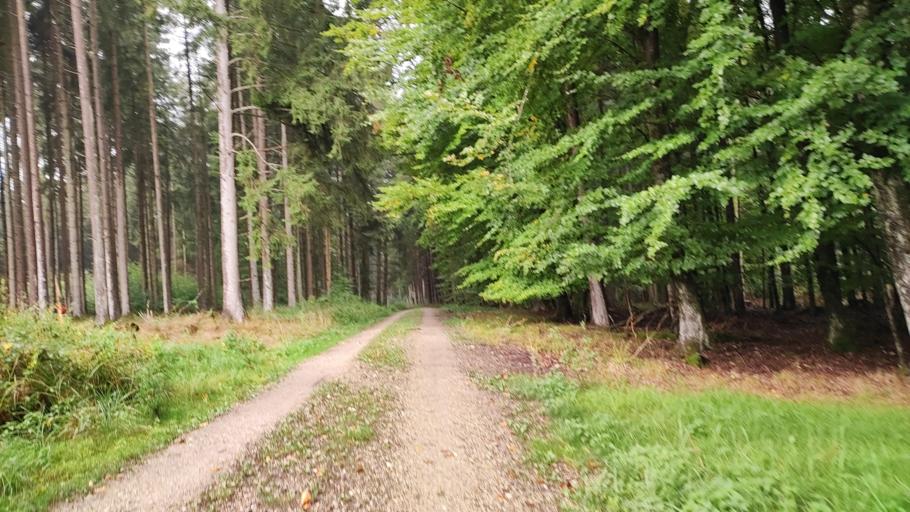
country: DE
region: Bavaria
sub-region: Swabia
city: Welden
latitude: 48.4292
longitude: 10.6303
